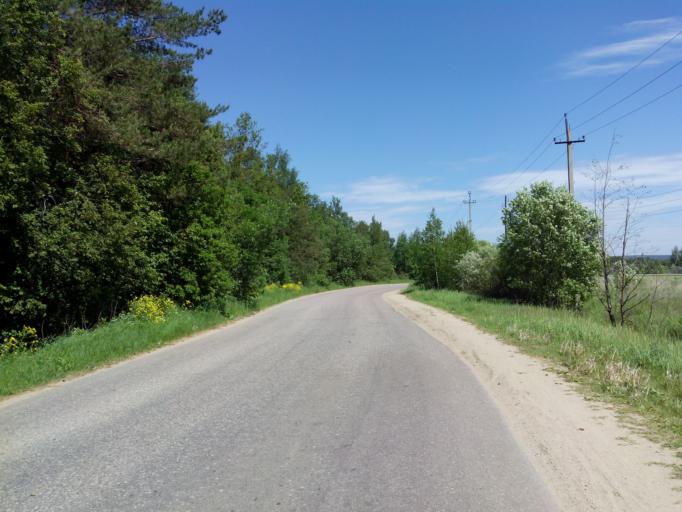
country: RU
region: Moskovskaya
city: Bogorodskoye
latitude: 56.5115
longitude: 38.1906
